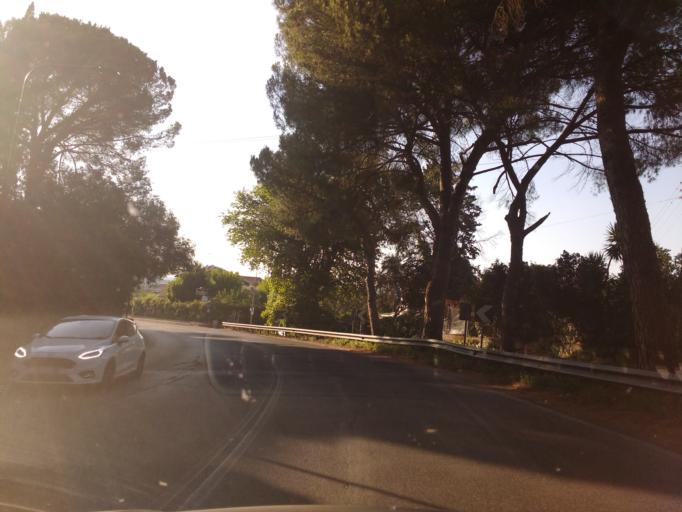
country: IT
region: Latium
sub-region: Citta metropolitana di Roma Capitale
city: Villa Adriana
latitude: 41.9560
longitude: 12.7834
